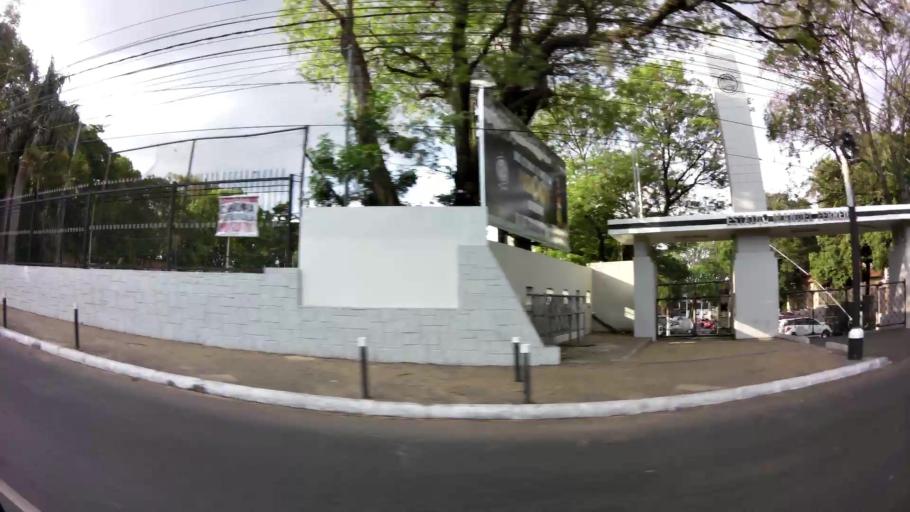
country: PY
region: Asuncion
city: Asuncion
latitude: -25.2935
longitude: -57.6090
